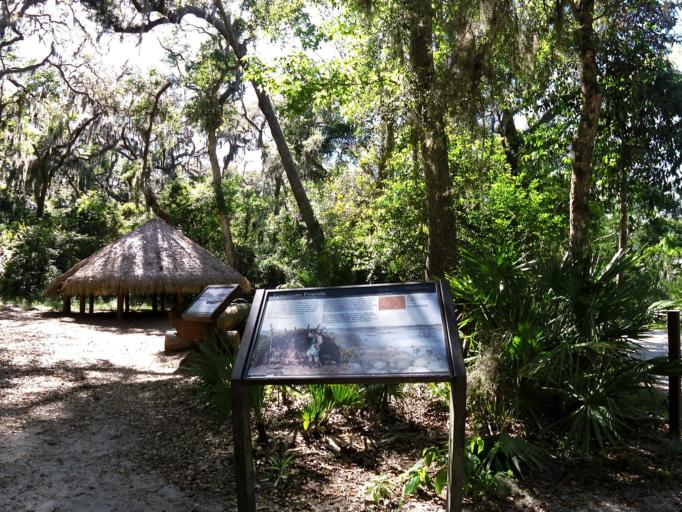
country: US
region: Florida
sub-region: Duval County
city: Atlantic Beach
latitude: 30.3863
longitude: -81.4985
